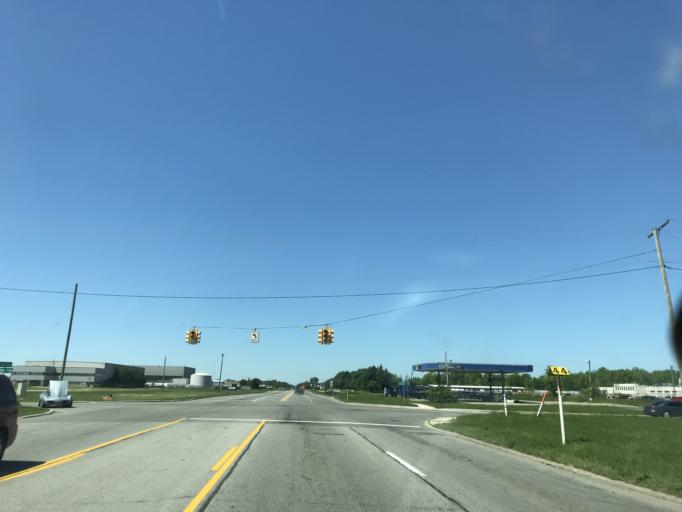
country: US
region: Michigan
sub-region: Wayne County
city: Taylor
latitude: 42.2239
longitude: -83.3273
